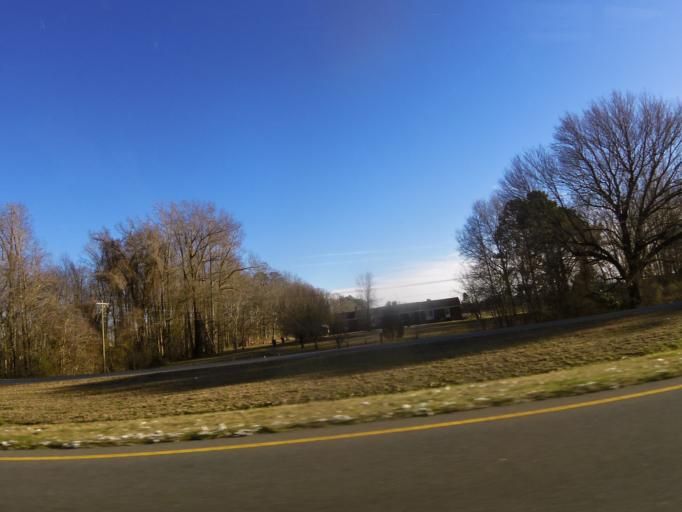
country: US
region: Virginia
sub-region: City of Franklin
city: Franklin
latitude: 36.6713
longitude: -76.7920
